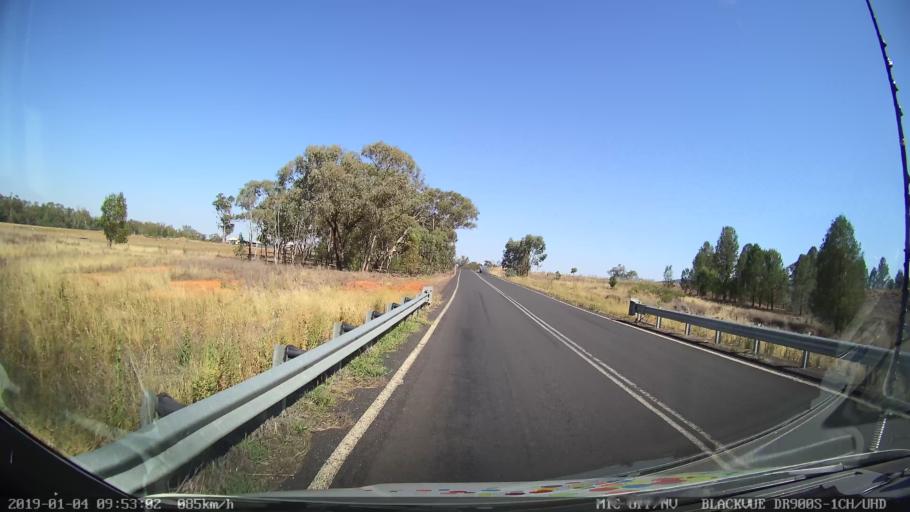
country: AU
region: New South Wales
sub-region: Cabonne
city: Canowindra
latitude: -33.5568
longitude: 148.4234
